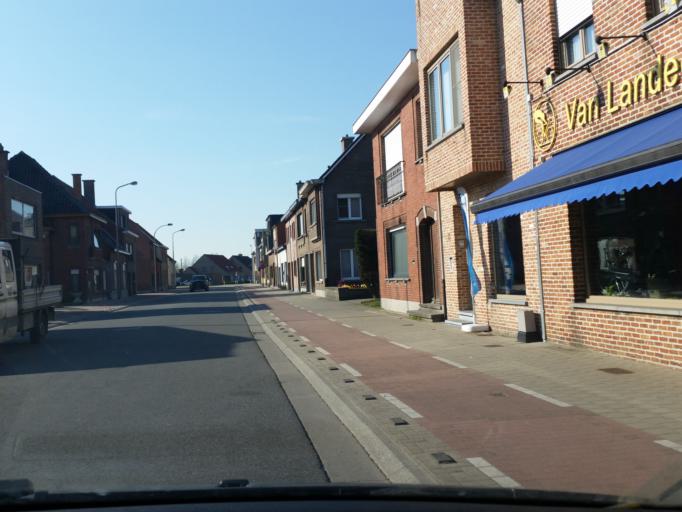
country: BE
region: Flanders
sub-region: Provincie Oost-Vlaanderen
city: Sint-Gillis-Waas
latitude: 51.2240
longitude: 4.1199
